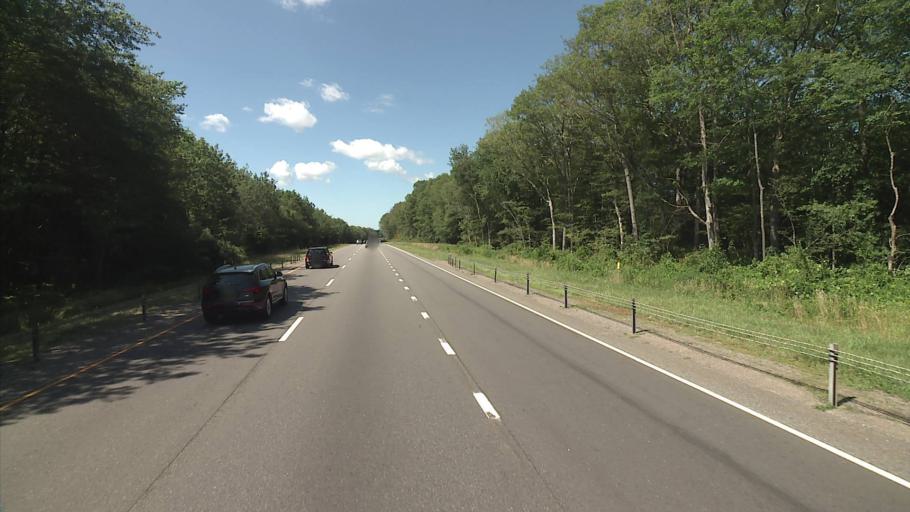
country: US
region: Rhode Island
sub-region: Washington County
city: Ashaway
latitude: 41.4354
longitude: -71.8085
